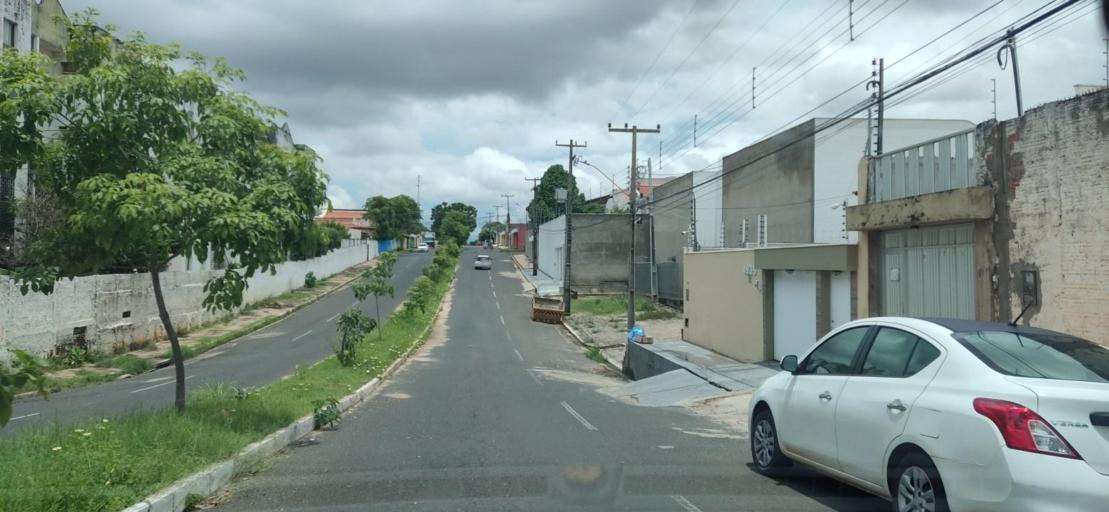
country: BR
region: Piaui
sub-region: Teresina
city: Teresina
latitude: -5.0745
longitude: -42.7564
